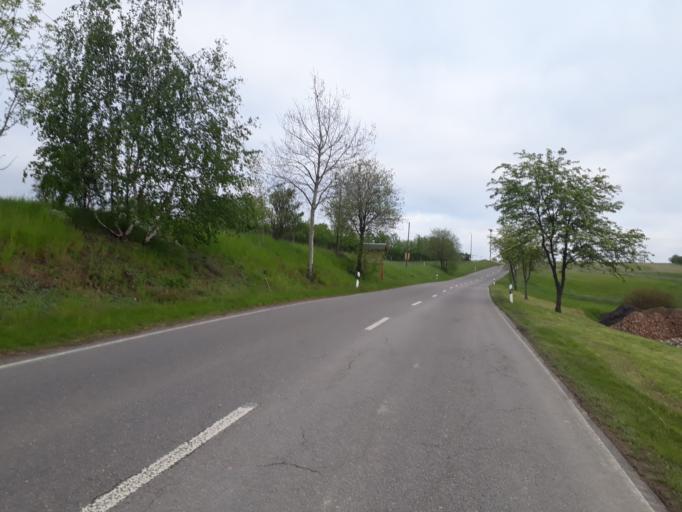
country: DE
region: Saxony
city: Reinhardtsgrimma
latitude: 50.8911
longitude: 13.7569
